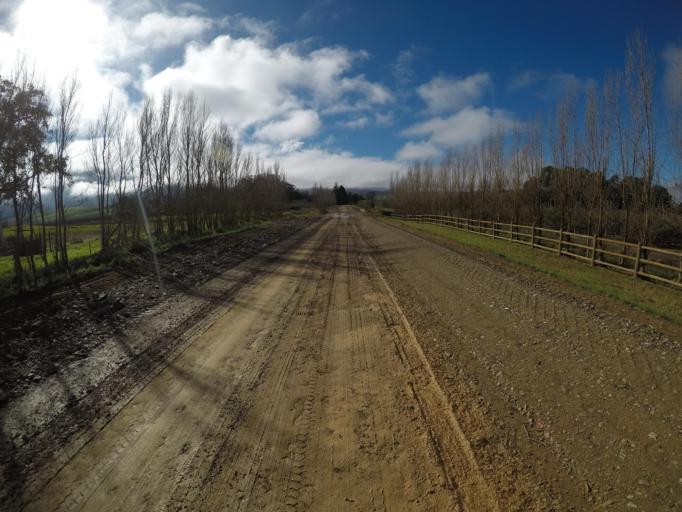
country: ZA
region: Western Cape
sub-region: Overberg District Municipality
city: Caledon
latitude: -34.1129
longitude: 19.7449
